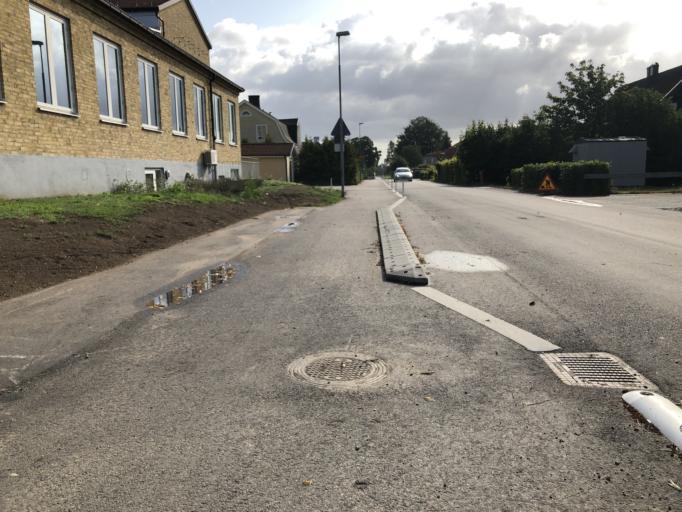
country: SE
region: Skane
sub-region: Hassleholms Kommun
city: Vinslov
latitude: 56.1008
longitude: 13.9161
